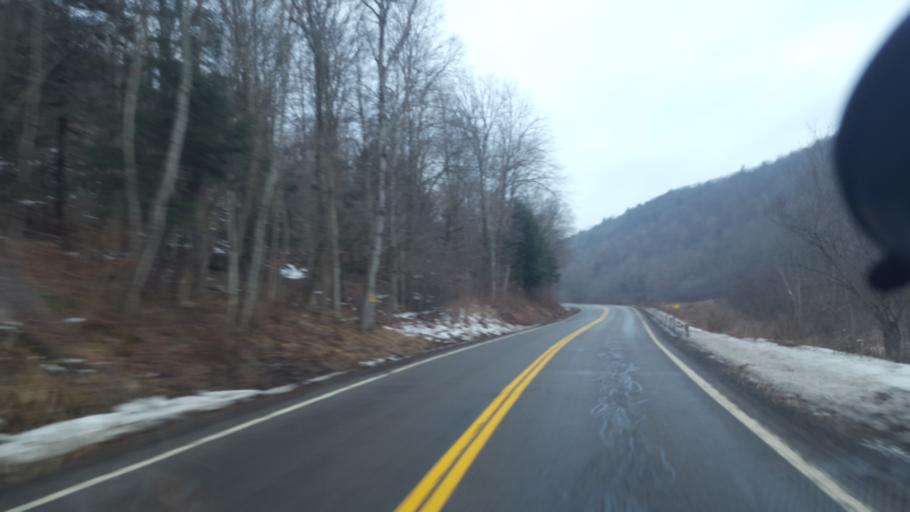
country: US
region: New York
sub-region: Allegany County
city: Andover
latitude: 42.0890
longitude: -77.6942
